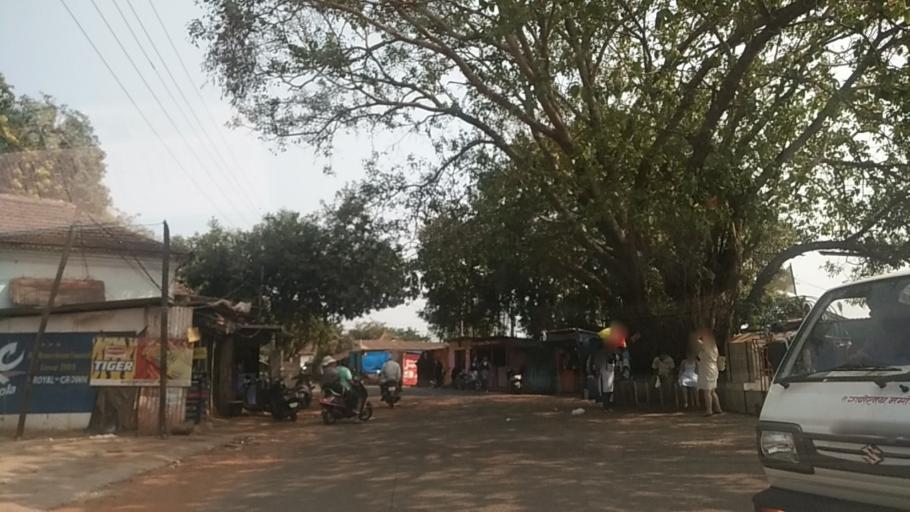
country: IN
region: Goa
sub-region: North Goa
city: Panaji
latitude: 15.5061
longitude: 73.8259
